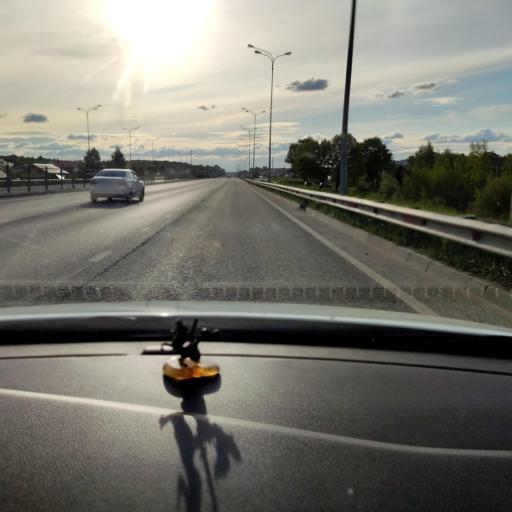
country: RU
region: Tatarstan
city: Osinovo
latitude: 55.8523
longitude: 48.8849
